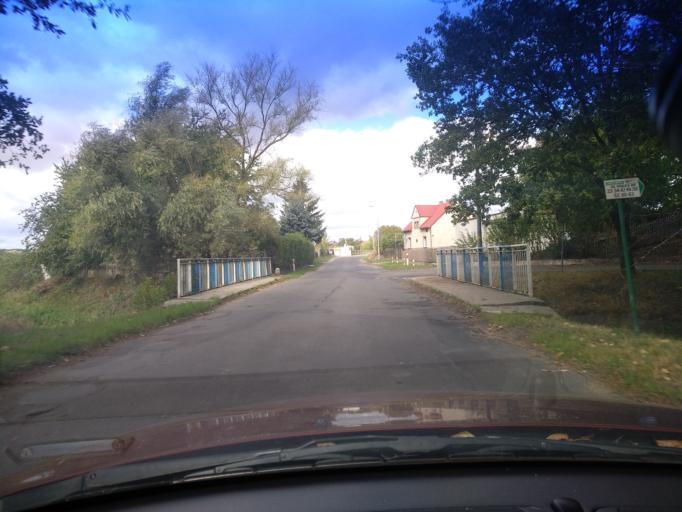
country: PL
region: Lower Silesian Voivodeship
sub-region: Powiat zgorzelecki
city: Zgorzelec
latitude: 51.1874
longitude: 15.0137
